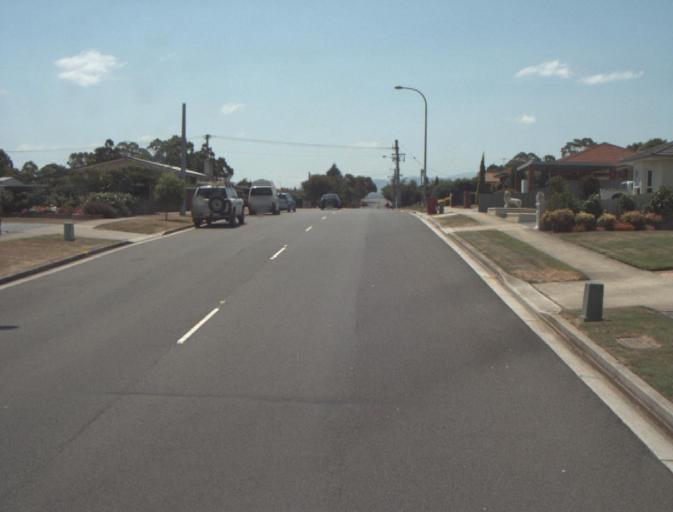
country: AU
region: Tasmania
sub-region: Launceston
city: Summerhill
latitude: -41.4893
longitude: 147.1746
